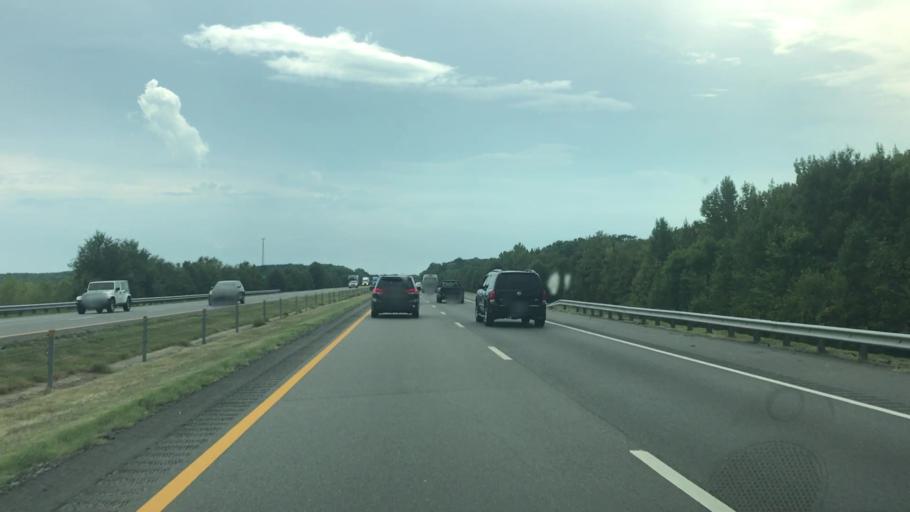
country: US
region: Arkansas
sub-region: Monroe County
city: Brinkley
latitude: 34.8832
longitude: -91.2622
